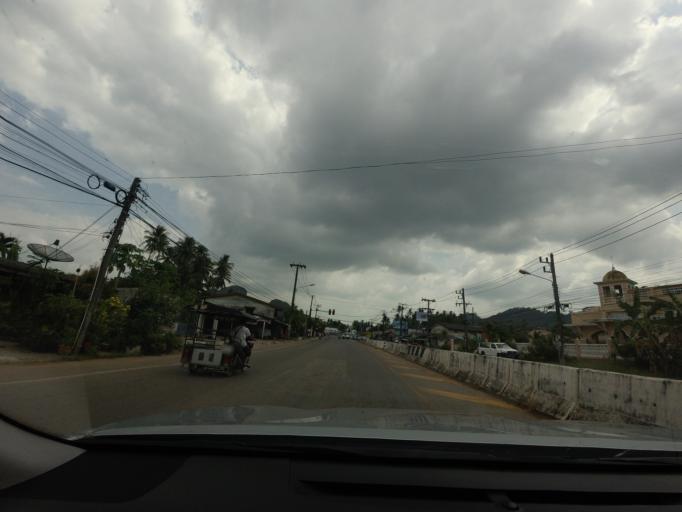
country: TH
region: Phangnga
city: Ban Ao Nang
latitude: 8.0931
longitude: 98.8112
